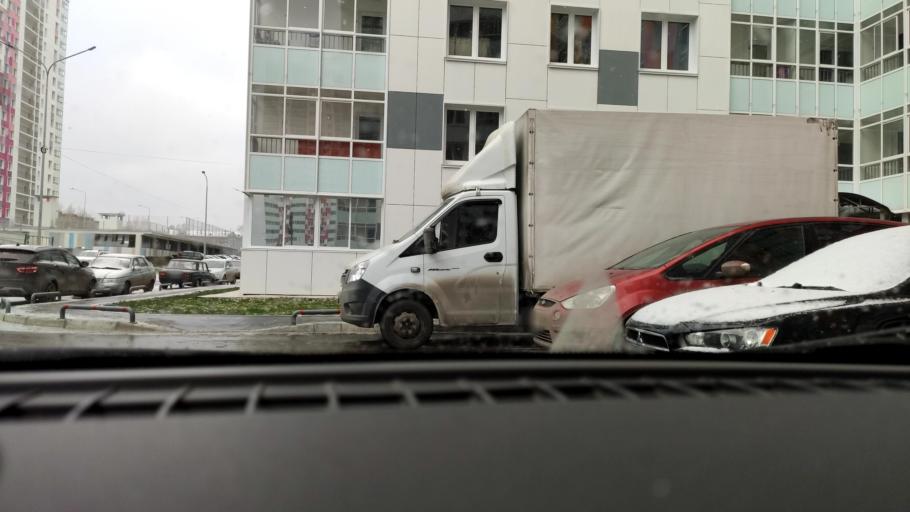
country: RU
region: Perm
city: Perm
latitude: 57.9907
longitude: 56.2654
